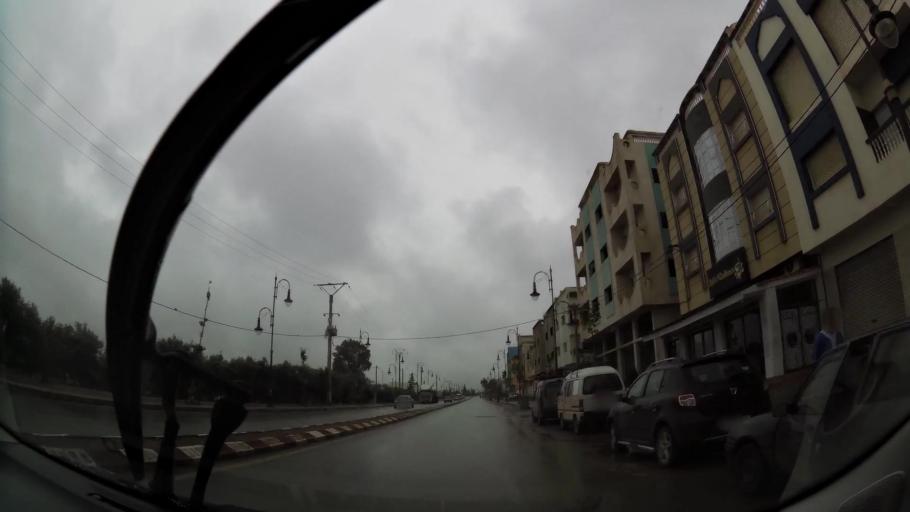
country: MA
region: Taza-Al Hoceima-Taounate
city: Imzourene
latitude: 35.1713
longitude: -3.8621
